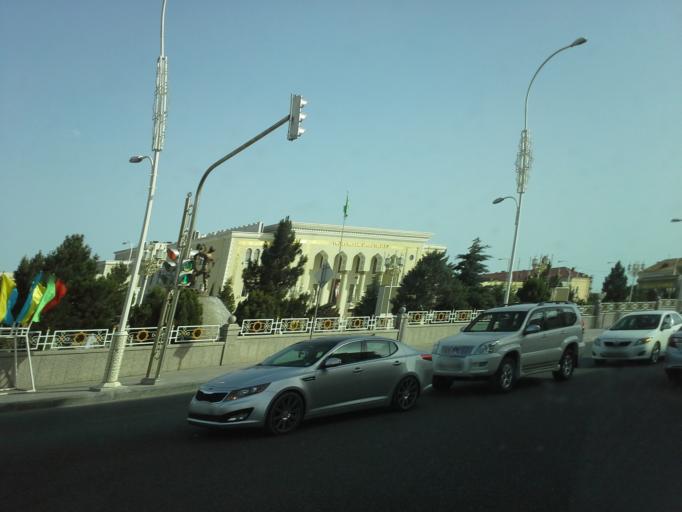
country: TM
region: Balkan
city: Turkmenbasy
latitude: 40.0062
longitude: 52.9936
